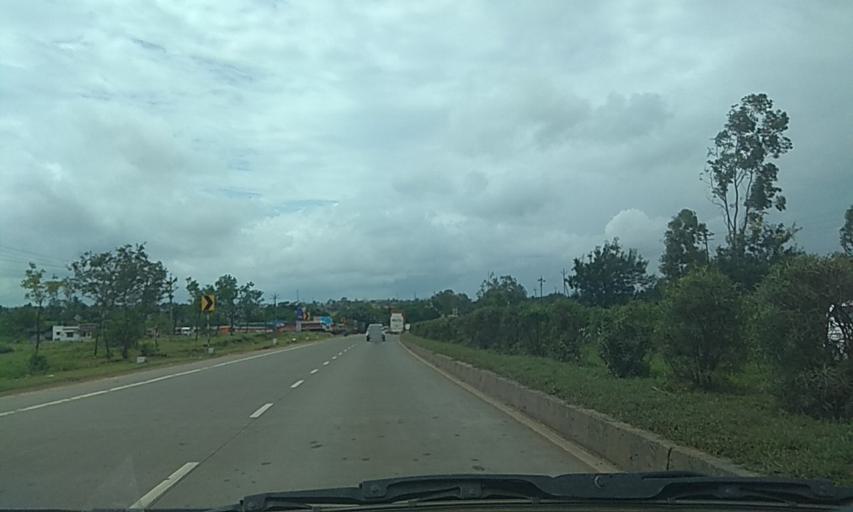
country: IN
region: Maharashtra
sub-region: Kolhapur
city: Kagal
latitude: 16.6229
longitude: 74.2955
